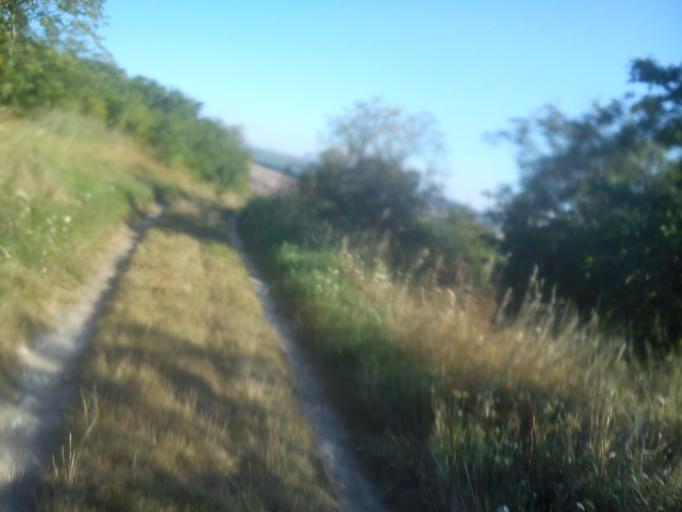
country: CZ
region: South Moravian
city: Sokolnice
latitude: 49.1116
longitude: 16.7664
